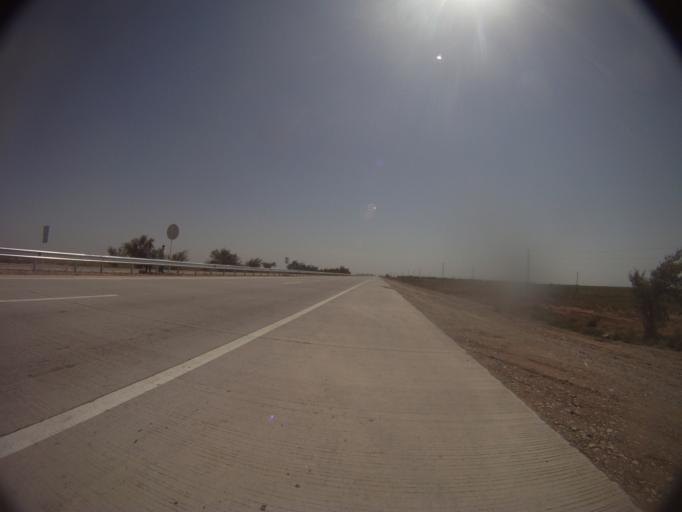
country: KZ
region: Ongtustik Qazaqstan
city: Bayaldyr
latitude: 43.0717
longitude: 68.6647
